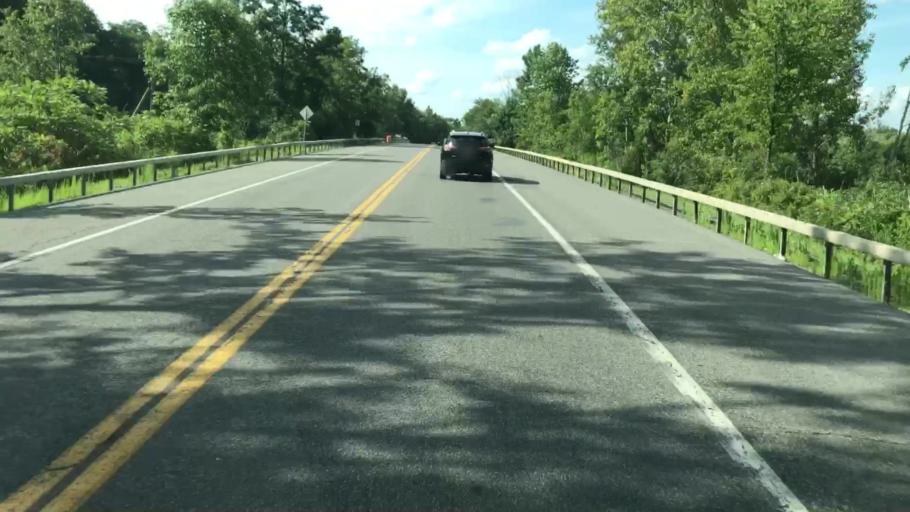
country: US
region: New York
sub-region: Onondaga County
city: Liverpool
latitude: 43.1700
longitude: -76.1969
